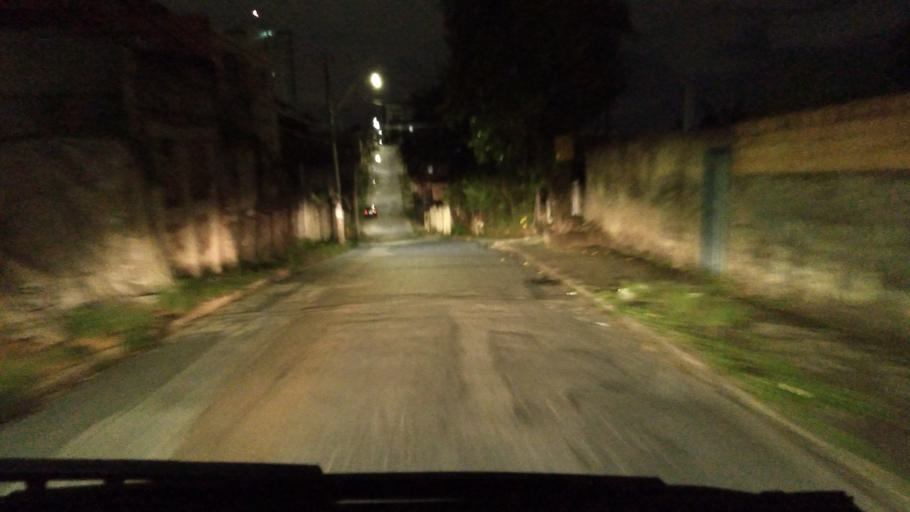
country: BR
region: Minas Gerais
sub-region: Belo Horizonte
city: Belo Horizonte
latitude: -19.8955
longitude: -43.9689
